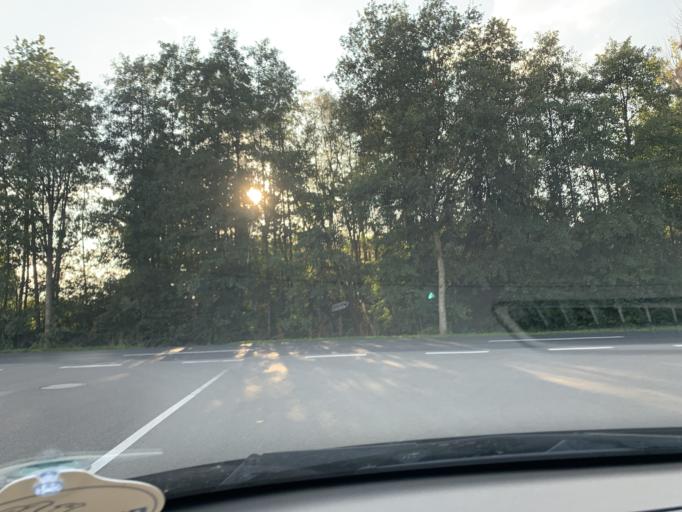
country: DE
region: Lower Saxony
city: Apen
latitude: 53.2630
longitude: 7.7545
